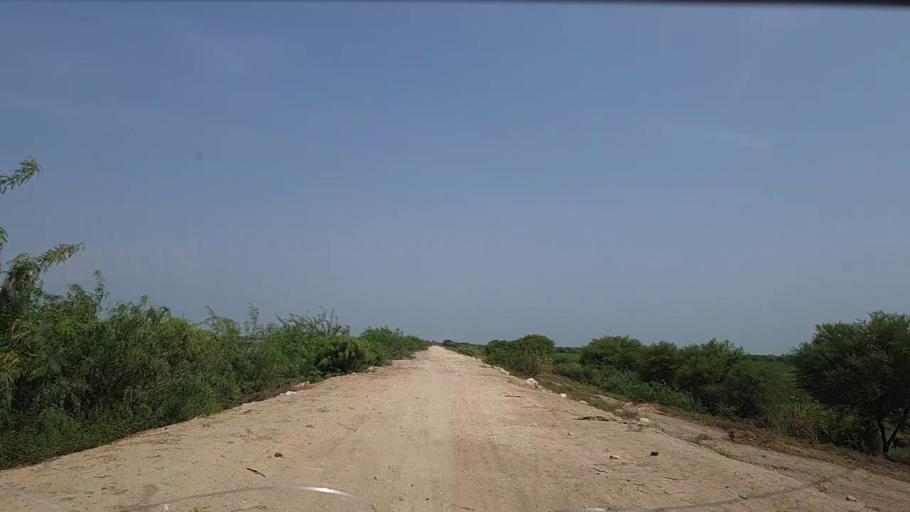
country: PK
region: Sindh
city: Ghotki
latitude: 28.1056
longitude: 69.3969
